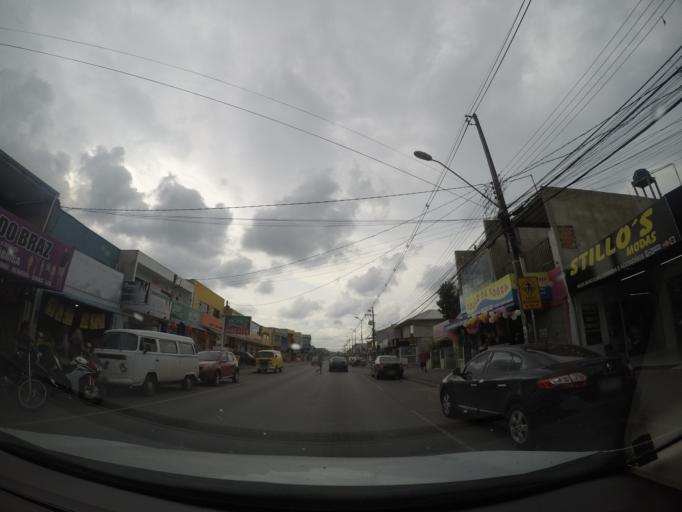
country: BR
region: Parana
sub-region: Sao Jose Dos Pinhais
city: Sao Jose dos Pinhais
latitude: -25.5523
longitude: -49.2498
